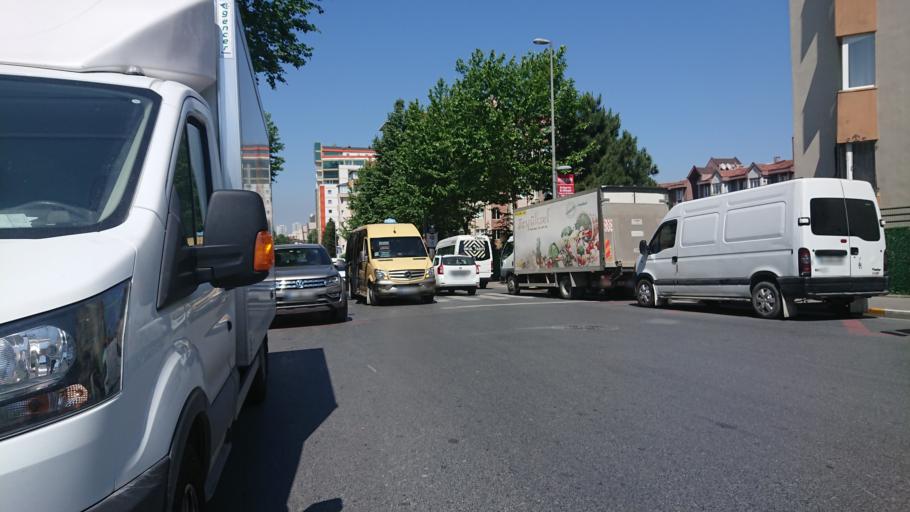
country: TR
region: Istanbul
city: Esenyurt
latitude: 41.0608
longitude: 28.6768
